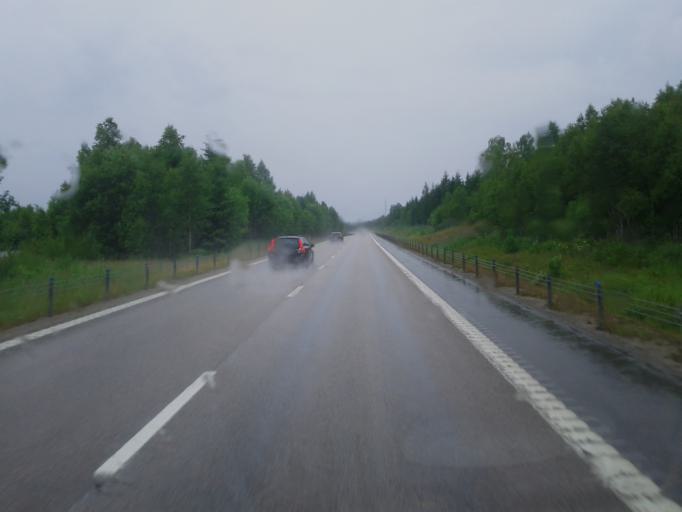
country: SE
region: Uppsala
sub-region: Tierps Kommun
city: Tierp
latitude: 60.3924
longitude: 17.4767
